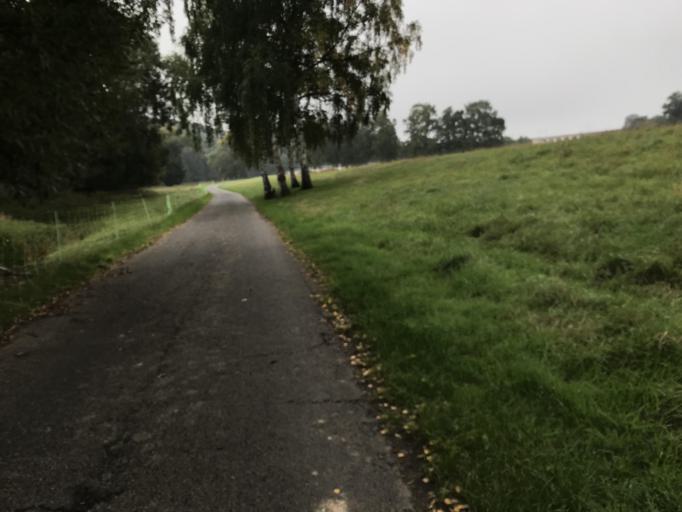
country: DE
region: Hesse
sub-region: Regierungsbezirk Kassel
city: Guxhagen
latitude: 51.2314
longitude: 9.4731
